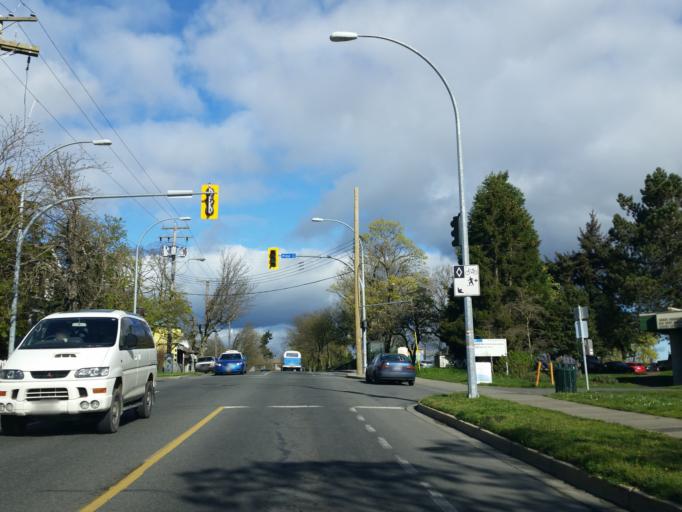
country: CA
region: British Columbia
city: Victoria
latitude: 48.4369
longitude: -123.3884
